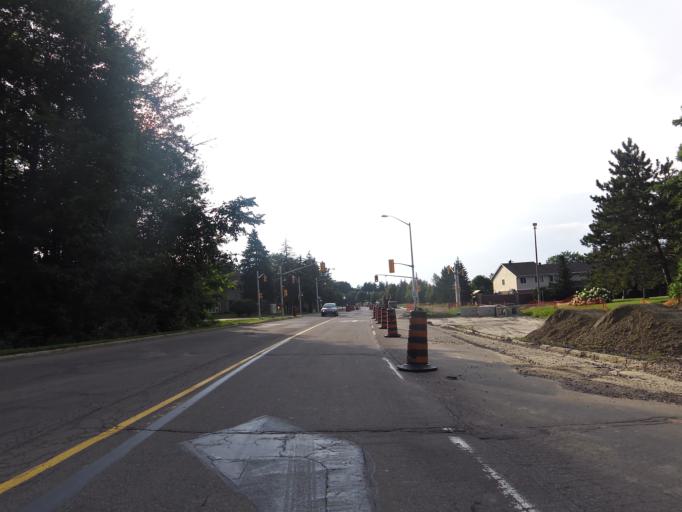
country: CA
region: Ontario
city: Bells Corners
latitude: 45.3145
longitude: -75.8850
